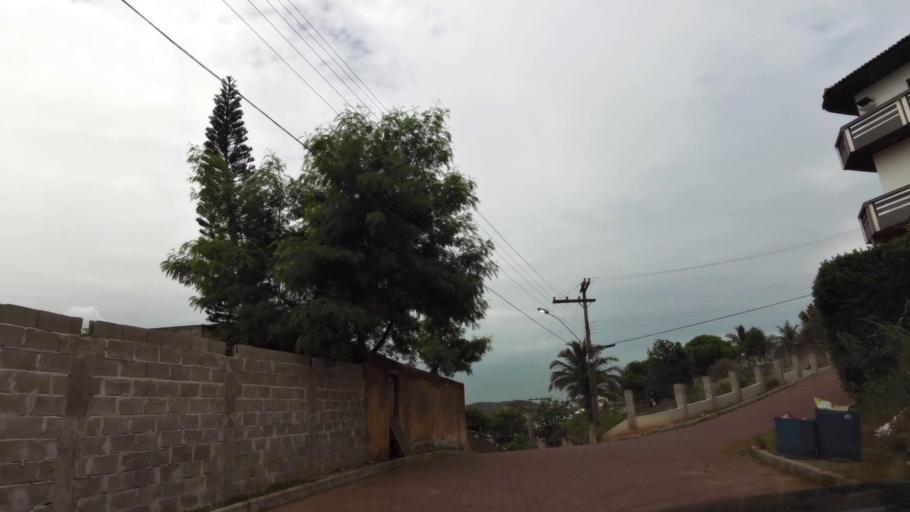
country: BR
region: Espirito Santo
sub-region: Guarapari
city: Guarapari
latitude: -20.6657
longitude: -40.4952
